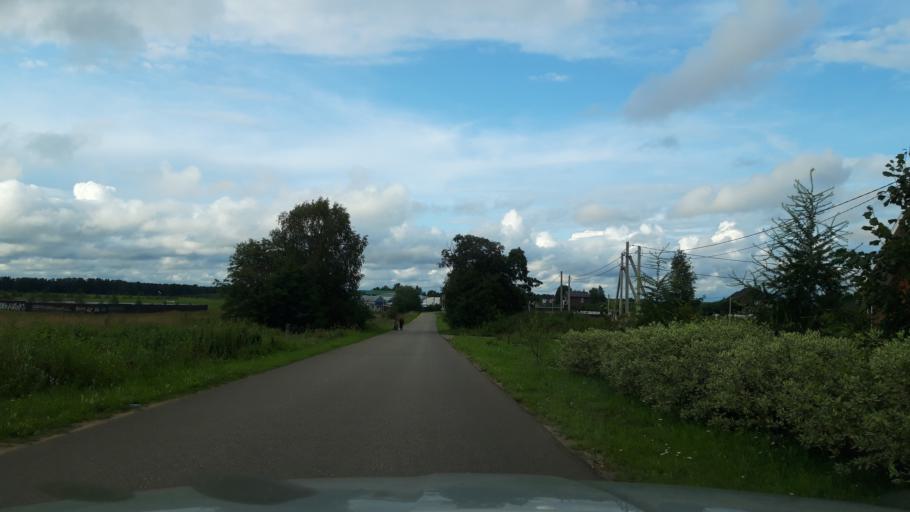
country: RU
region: Moskovskaya
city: Istra
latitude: 56.0970
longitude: 36.7984
